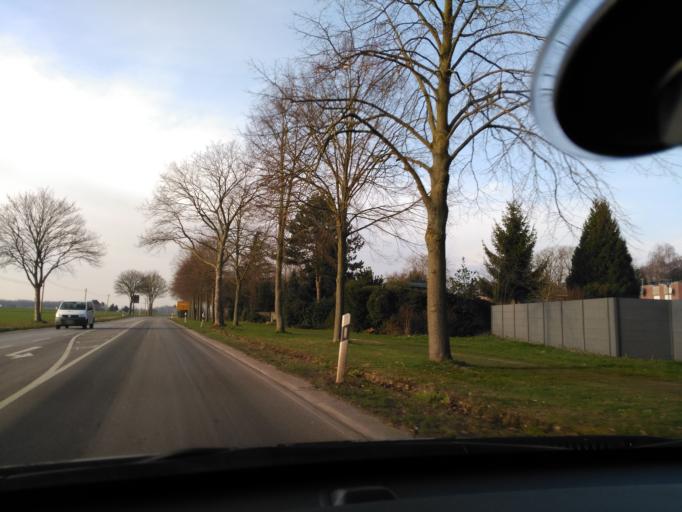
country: DE
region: North Rhine-Westphalia
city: Wegberg
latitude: 51.1452
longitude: 6.3662
